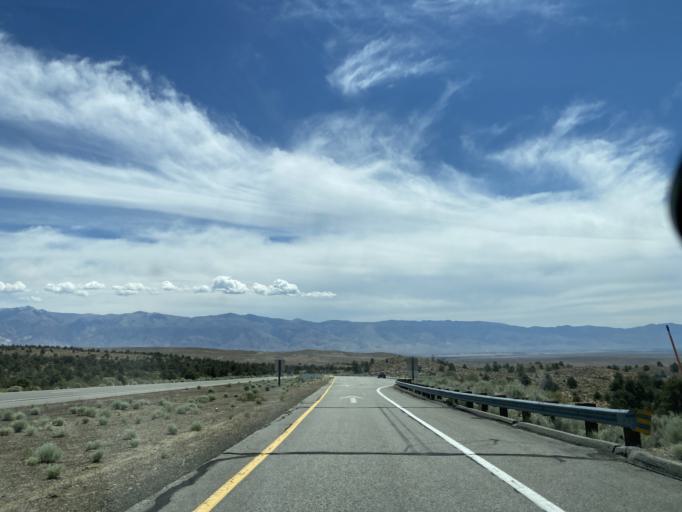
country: US
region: California
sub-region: Inyo County
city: West Bishop
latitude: 37.5192
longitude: -118.6058
